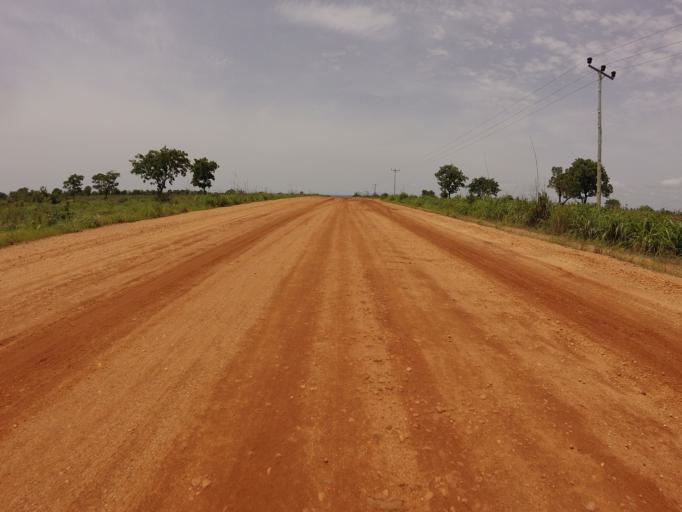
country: GH
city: Kpandae
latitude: 8.7305
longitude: 0.1080
